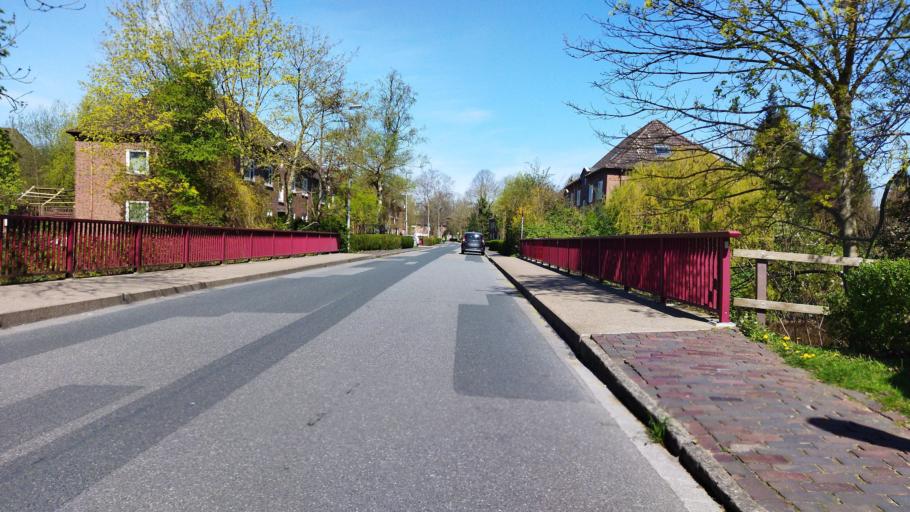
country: DE
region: Lower Saxony
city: Brake (Unterweser)
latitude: 53.3338
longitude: 8.4853
